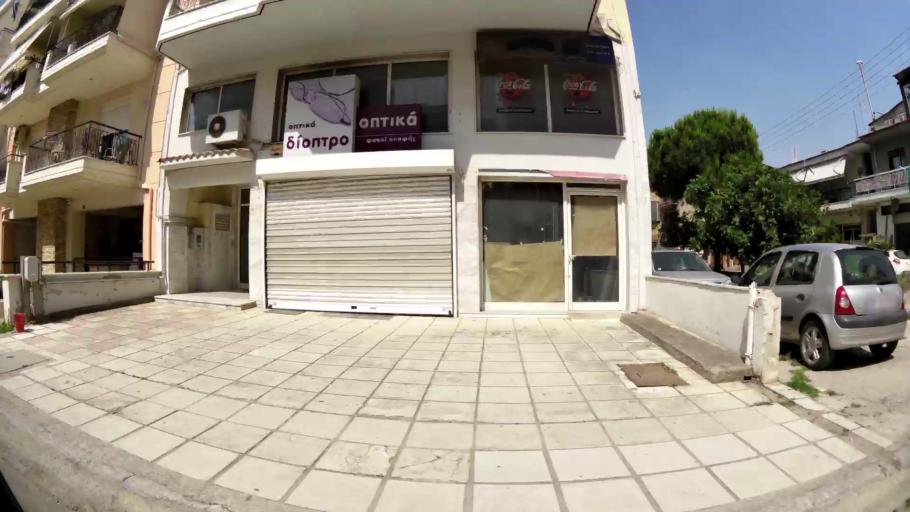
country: GR
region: Central Macedonia
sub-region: Nomos Thessalonikis
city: Evosmos
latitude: 40.6694
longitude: 22.9202
